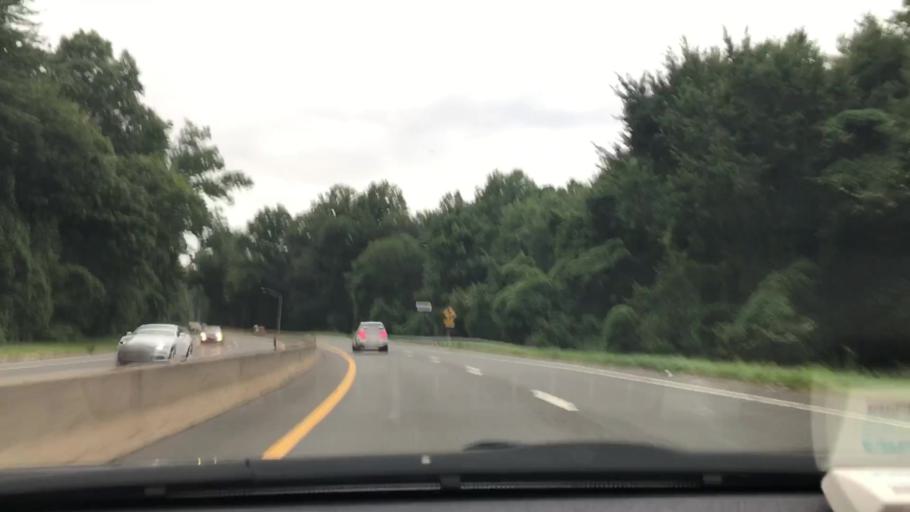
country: US
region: New York
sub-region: Westchester County
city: Pelham
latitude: 40.9292
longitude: -73.8027
